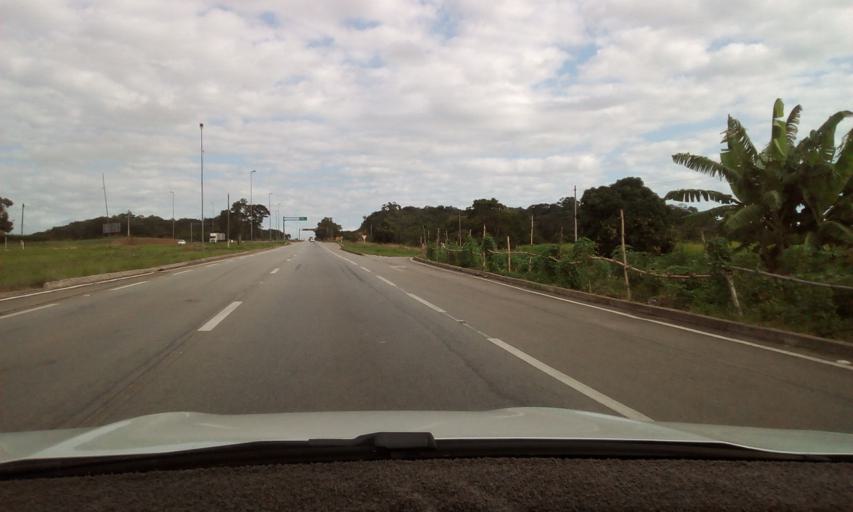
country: BR
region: Paraiba
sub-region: Mamanguape
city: Mamanguape
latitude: -6.8598
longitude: -35.1342
